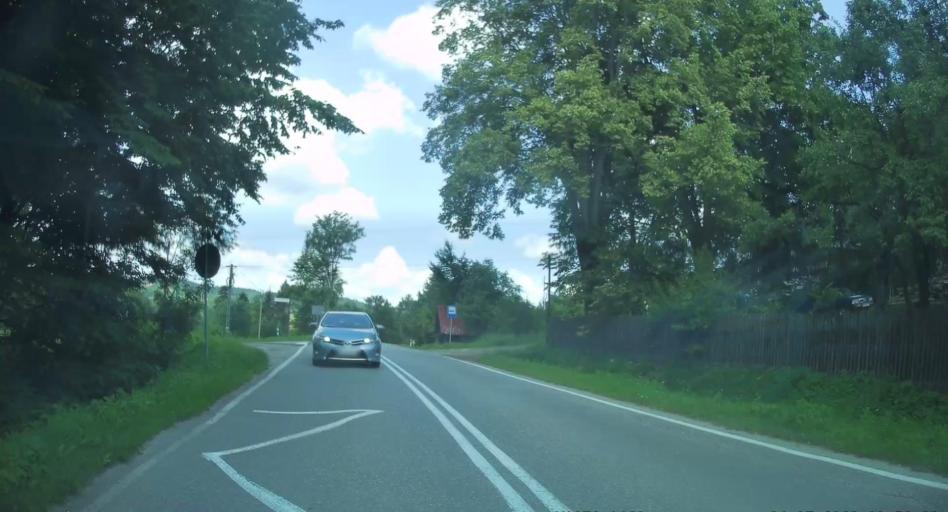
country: PL
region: Lesser Poland Voivodeship
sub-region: Powiat tarnowski
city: Zakliczyn
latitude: 49.7677
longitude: 20.7807
